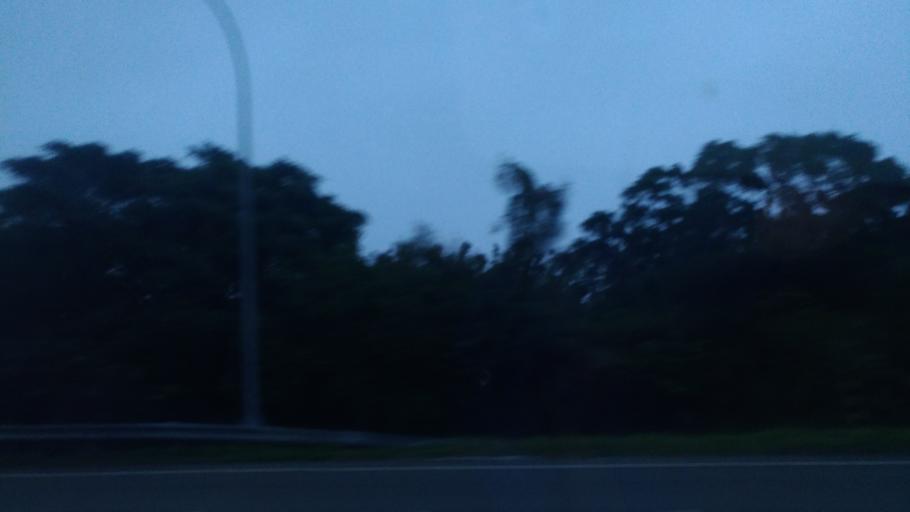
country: TW
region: Taiwan
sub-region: Hsinchu
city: Hsinchu
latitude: 24.7293
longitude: 120.9036
